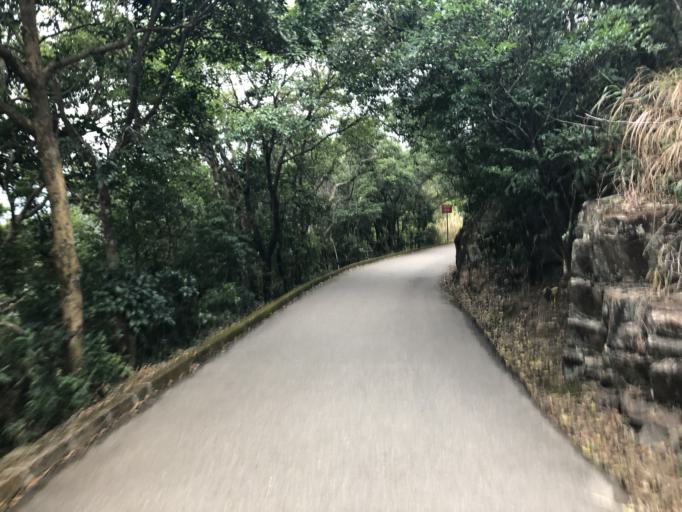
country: HK
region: Wanchai
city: Wan Chai
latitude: 22.2663
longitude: 114.2127
